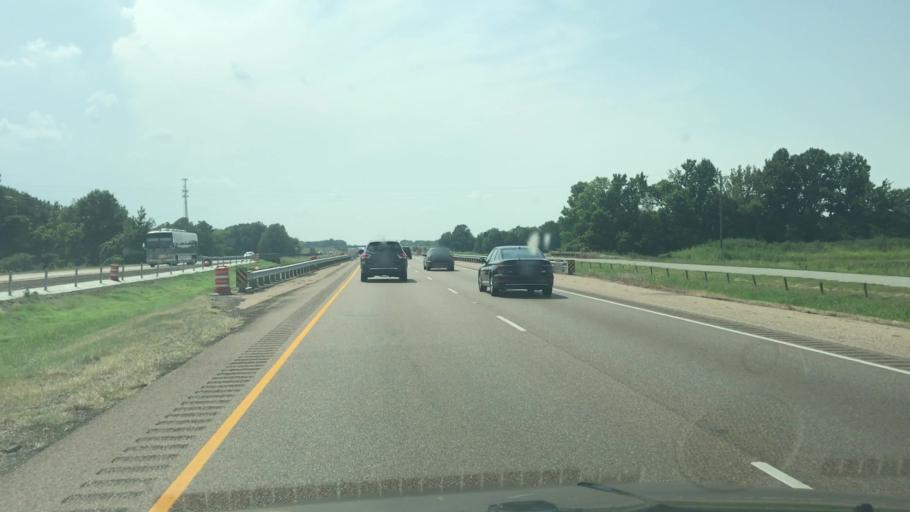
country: US
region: Arkansas
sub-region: Crittenden County
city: Earle
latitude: 35.1495
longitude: -90.3537
